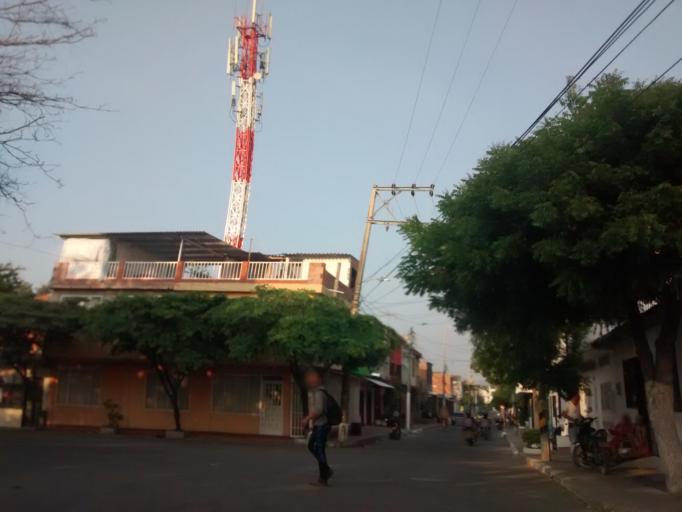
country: CO
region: Cundinamarca
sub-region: Girardot
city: Girardot City
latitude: 4.3155
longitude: -74.7861
